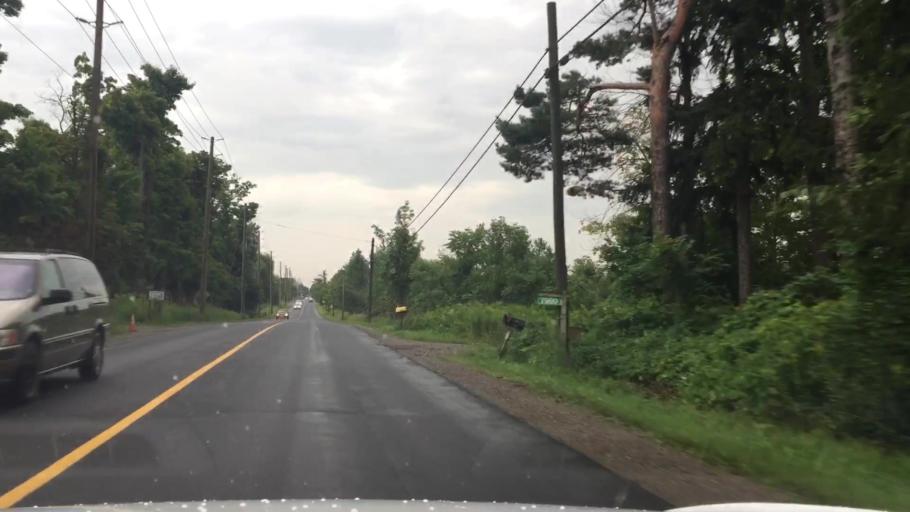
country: CA
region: Ontario
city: Markham
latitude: 43.8708
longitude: -79.2072
